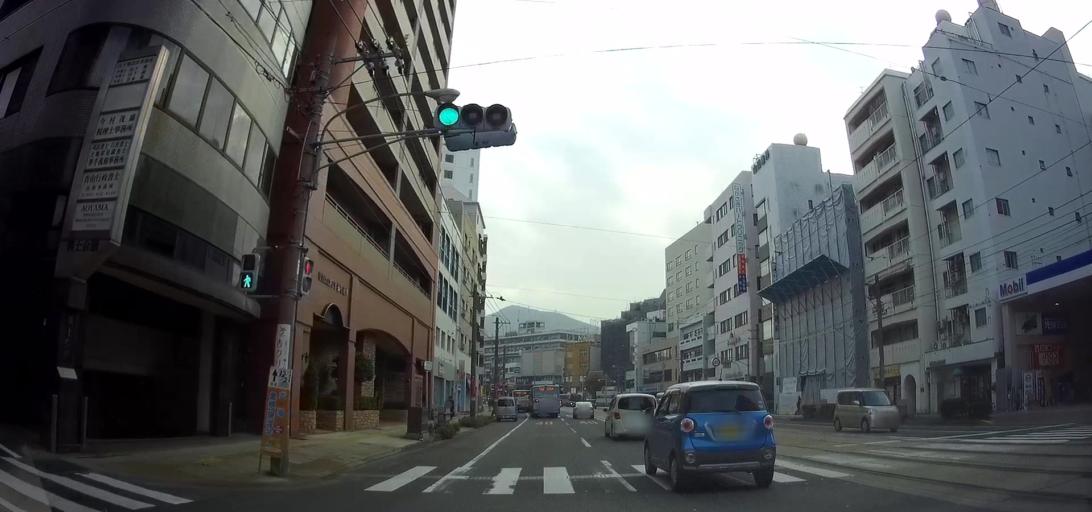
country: JP
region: Nagasaki
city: Nagasaki-shi
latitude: 32.7510
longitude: 129.8749
